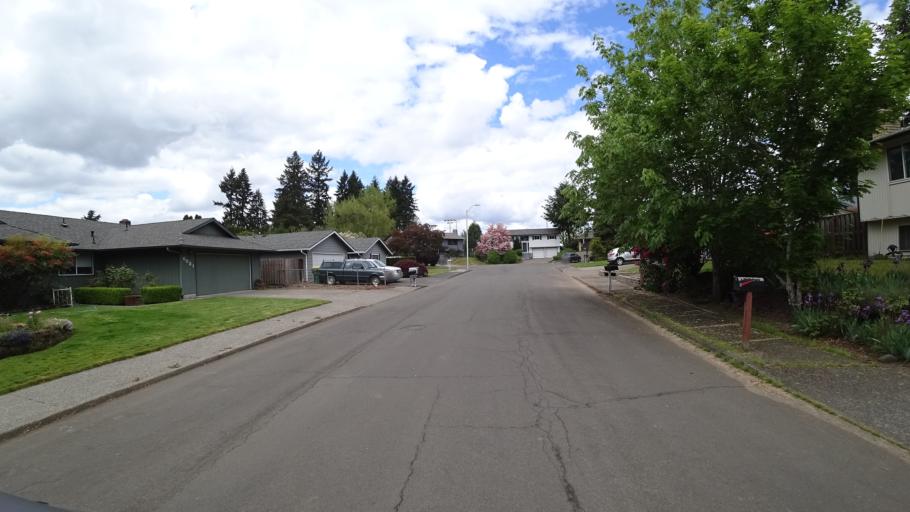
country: US
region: Oregon
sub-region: Washington County
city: Aloha
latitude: 45.4760
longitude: -122.8549
